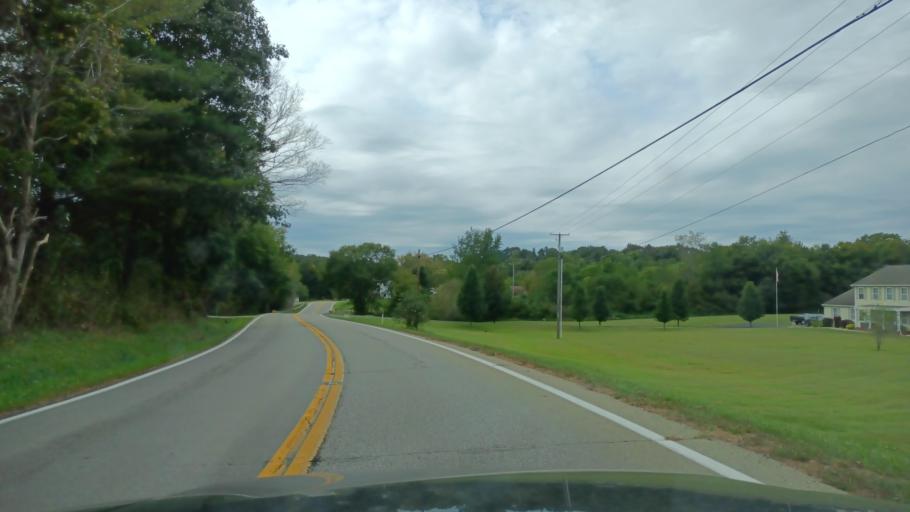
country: US
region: Ohio
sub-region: Vinton County
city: McArthur
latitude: 39.2716
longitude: -82.5194
